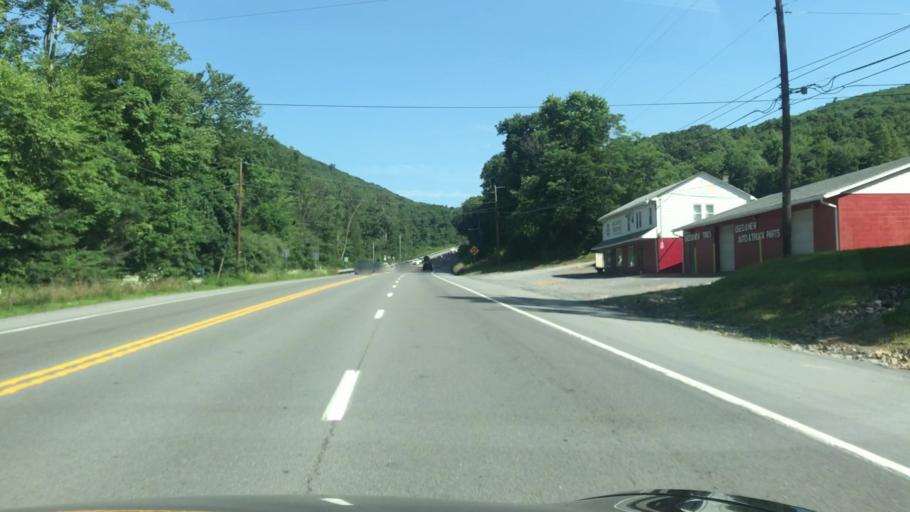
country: US
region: Pennsylvania
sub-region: Lycoming County
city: Montgomery
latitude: 41.1975
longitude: -76.9181
